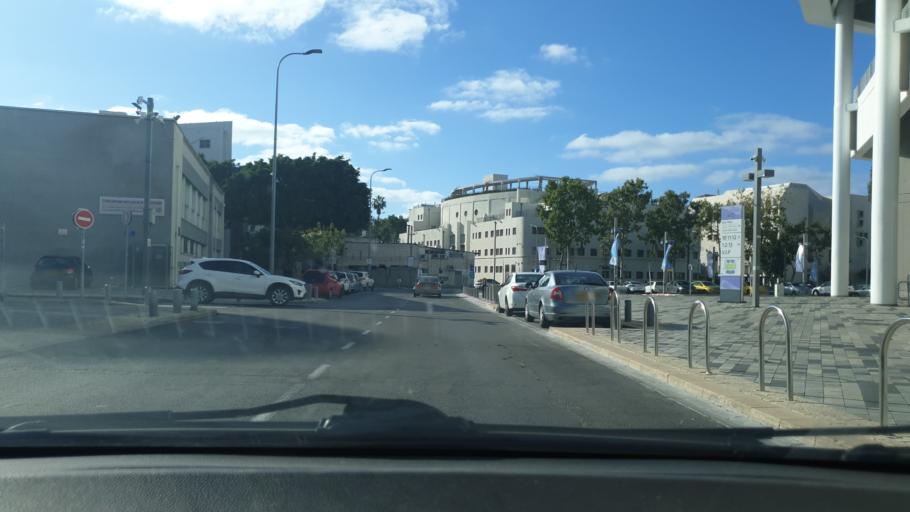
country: IL
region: Tel Aviv
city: Yafo
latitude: 32.0512
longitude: 34.7607
